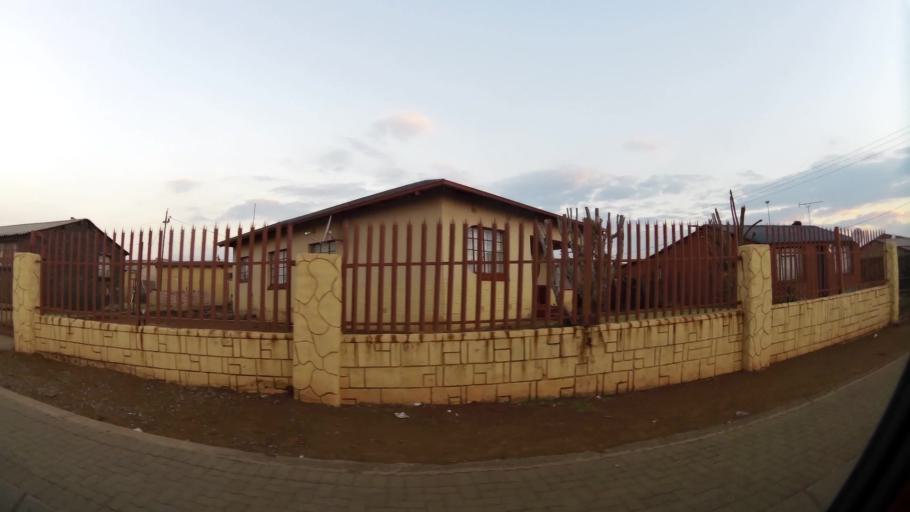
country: ZA
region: Gauteng
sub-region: City of Johannesburg Metropolitan Municipality
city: Orange Farm
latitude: -26.5559
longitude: 27.8764
